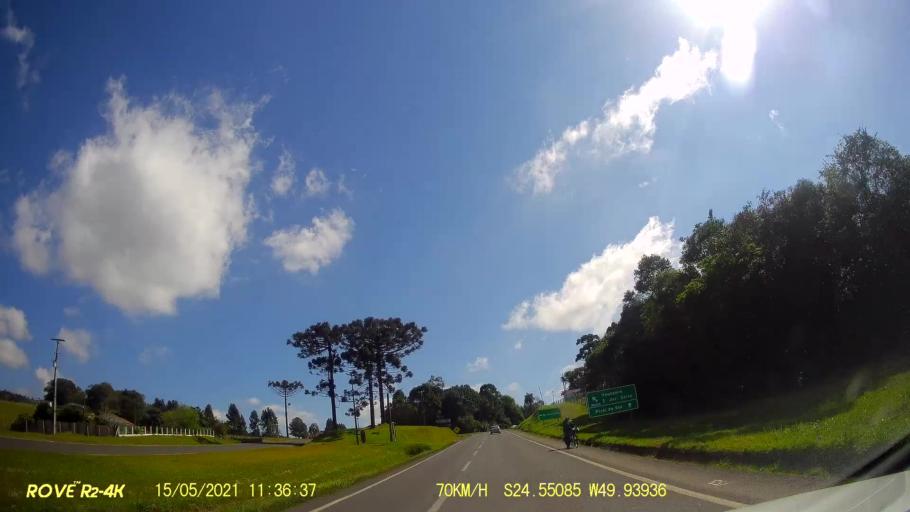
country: BR
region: Parana
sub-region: Pirai Do Sul
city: Pirai do Sul
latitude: -24.5508
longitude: -49.9393
